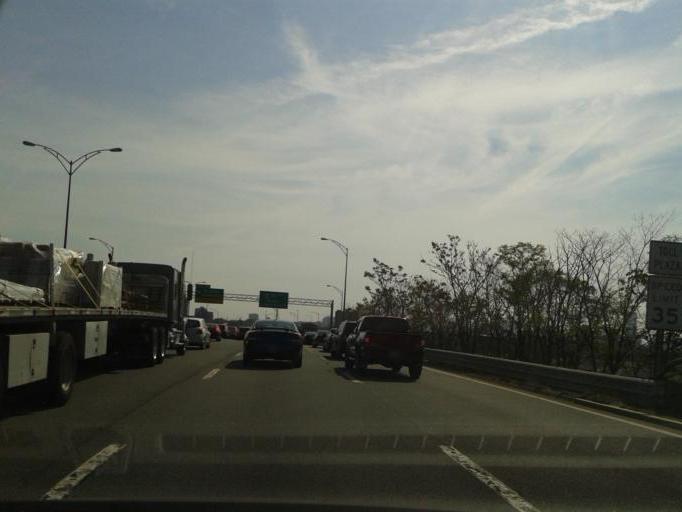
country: US
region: Massachusetts
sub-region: Norfolk County
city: Brookline
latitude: 42.3567
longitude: -71.1274
